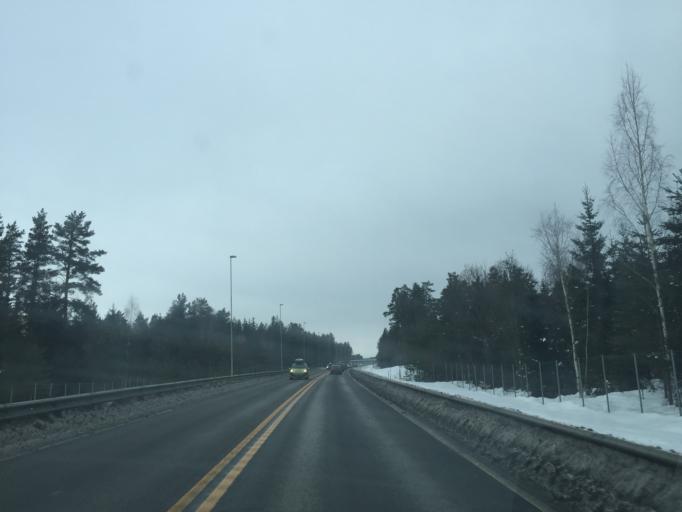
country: NO
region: Hedmark
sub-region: Loten
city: Loten
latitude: 60.7510
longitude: 11.3015
